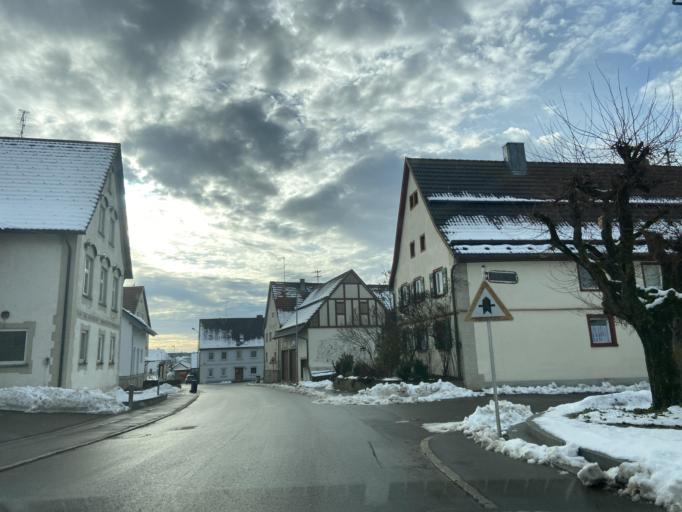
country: DE
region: Baden-Wuerttemberg
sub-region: Tuebingen Region
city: Trochtelfingen
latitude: 48.2683
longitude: 9.2770
